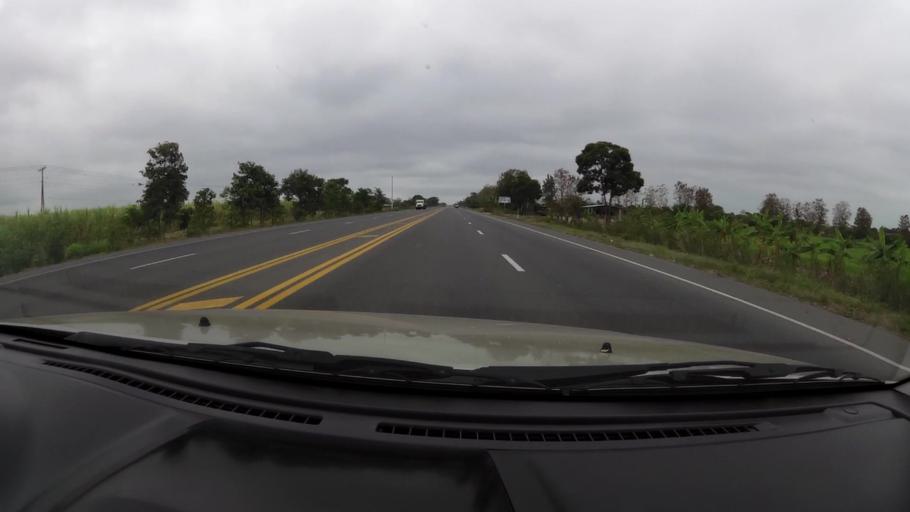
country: EC
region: Guayas
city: Naranjal
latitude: -2.4880
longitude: -79.6104
